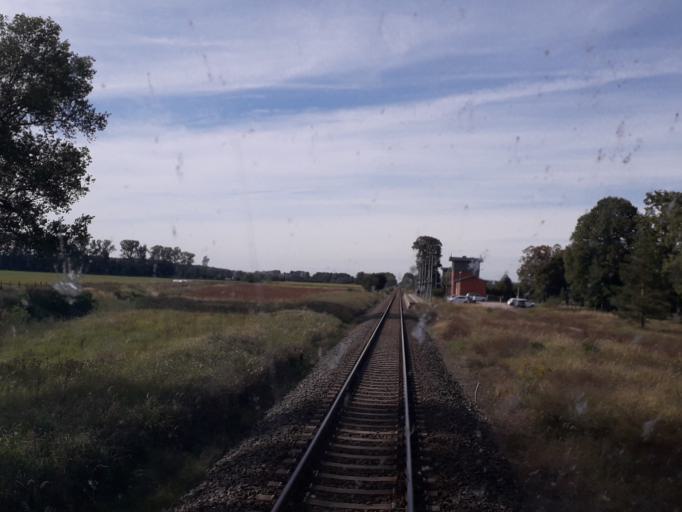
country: DE
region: Brandenburg
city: Kremmen
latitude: 52.8036
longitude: 13.0238
